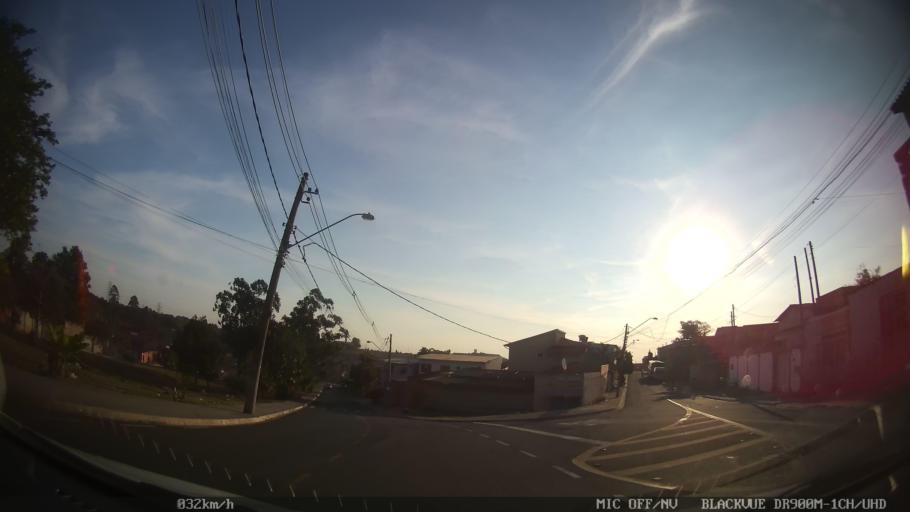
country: BR
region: Sao Paulo
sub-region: Campinas
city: Campinas
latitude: -22.9915
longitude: -47.1222
